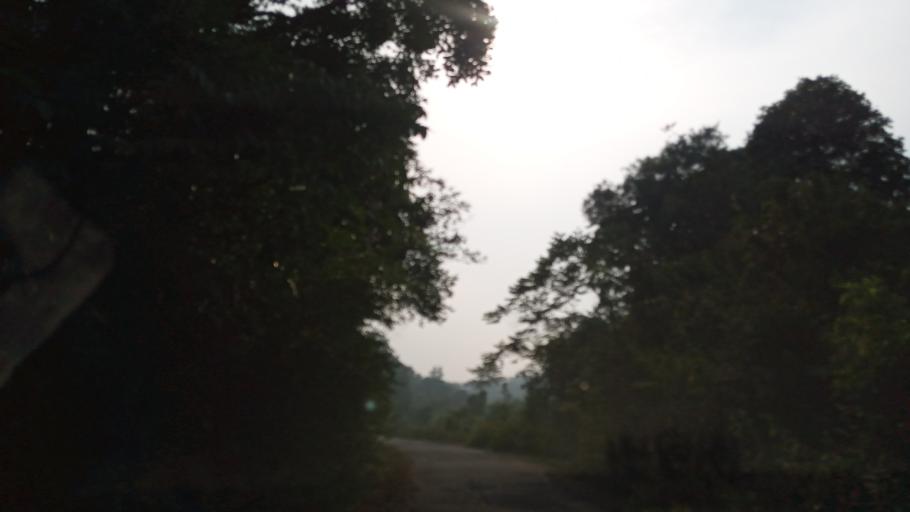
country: IN
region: Karnataka
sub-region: Chikmagalur
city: Mudigere
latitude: 13.0021
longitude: 75.6246
